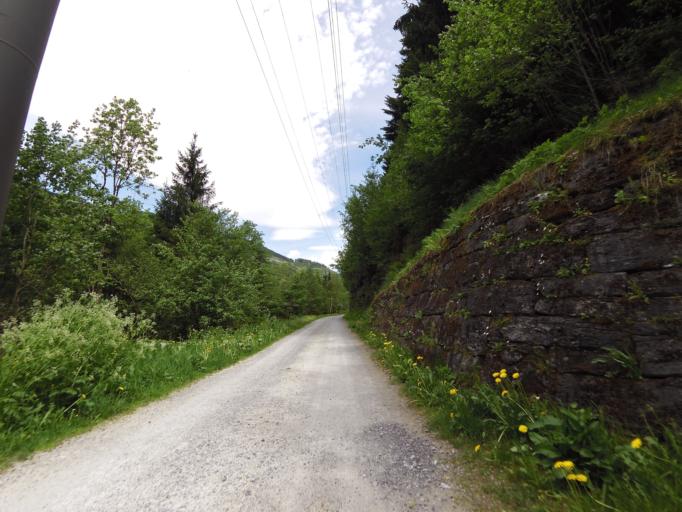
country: CH
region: Grisons
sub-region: Surselva District
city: Ilanz
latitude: 46.7734
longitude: 9.1451
